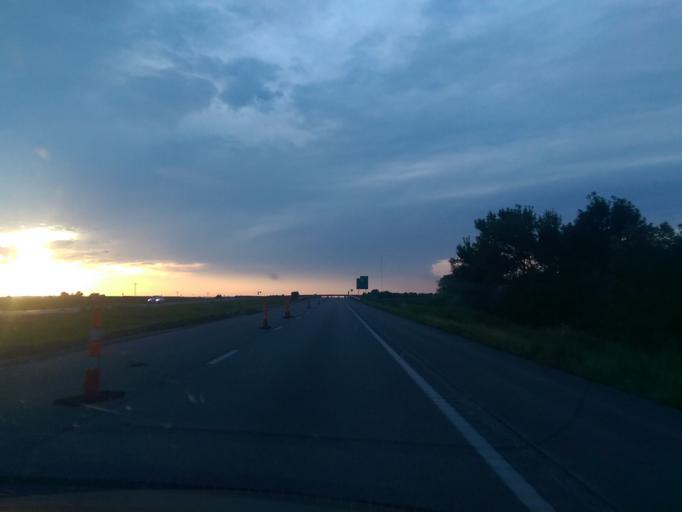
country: US
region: Missouri
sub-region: Atchison County
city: Rock Port
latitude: 40.3626
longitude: -95.5240
